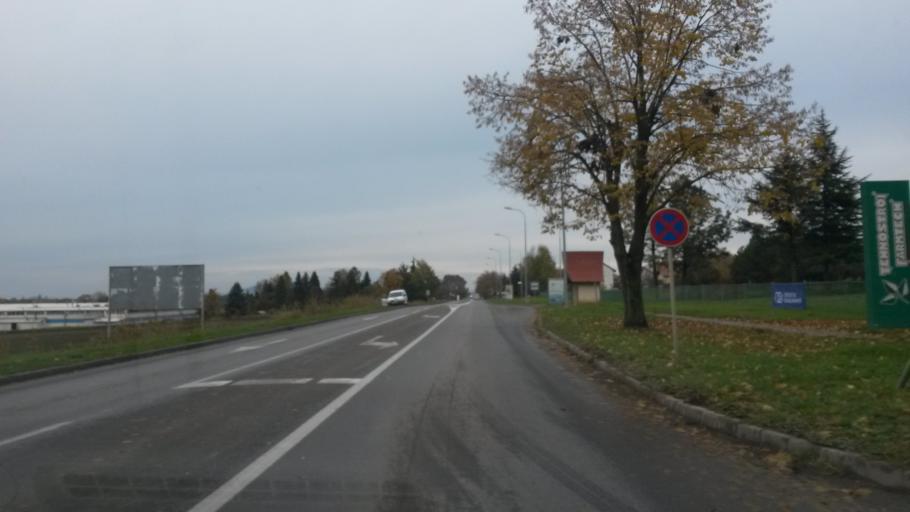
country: HR
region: Osjecko-Baranjska
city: Beli Manastir
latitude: 45.7621
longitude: 18.6247
